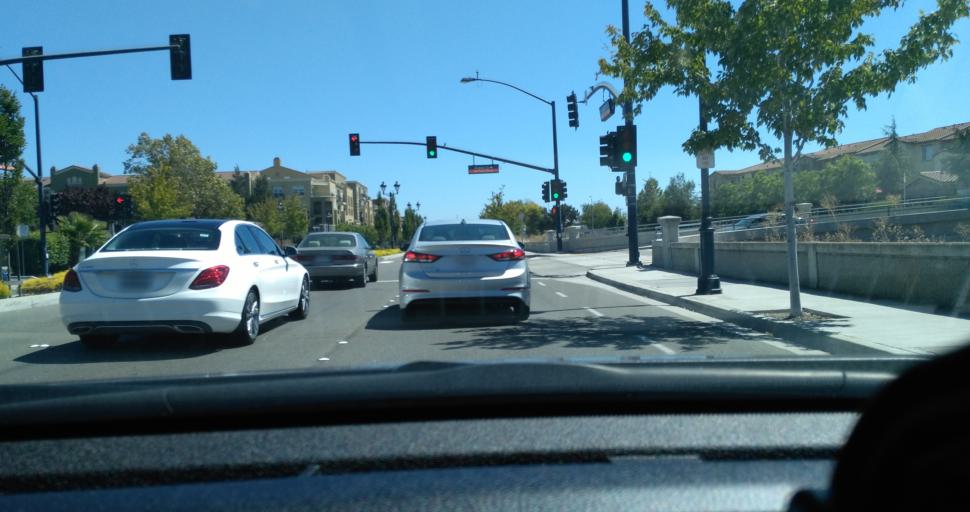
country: US
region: California
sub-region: Santa Clara County
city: Milpitas
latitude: 37.4233
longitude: -121.9070
